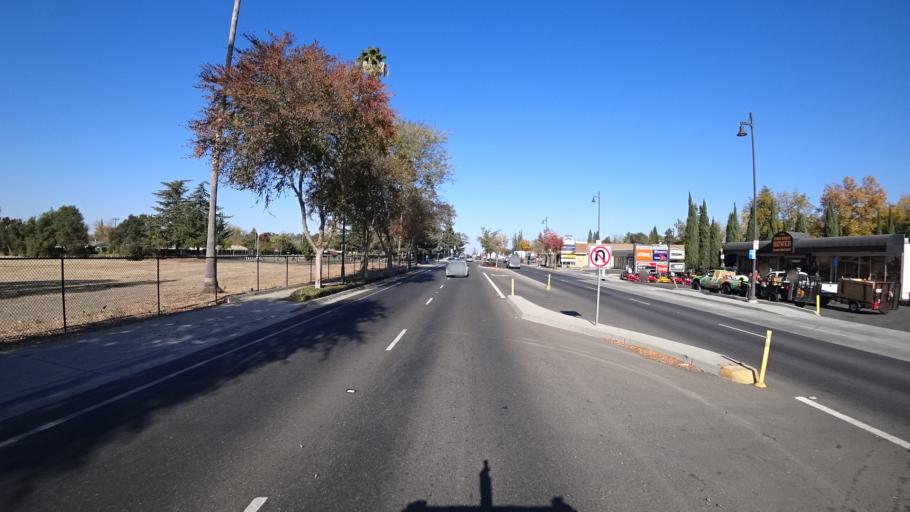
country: US
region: California
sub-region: Sacramento County
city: Citrus Heights
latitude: 38.6971
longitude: -121.2903
